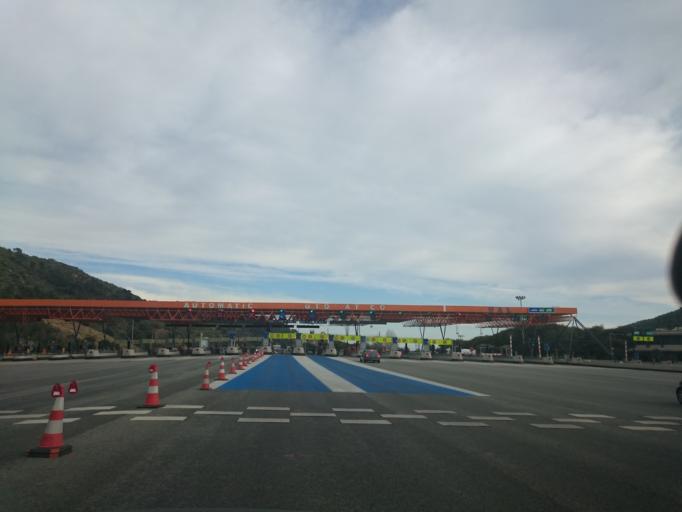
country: ES
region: Catalonia
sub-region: Provincia de Barcelona
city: Sitges
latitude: 41.2453
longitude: 1.8510
